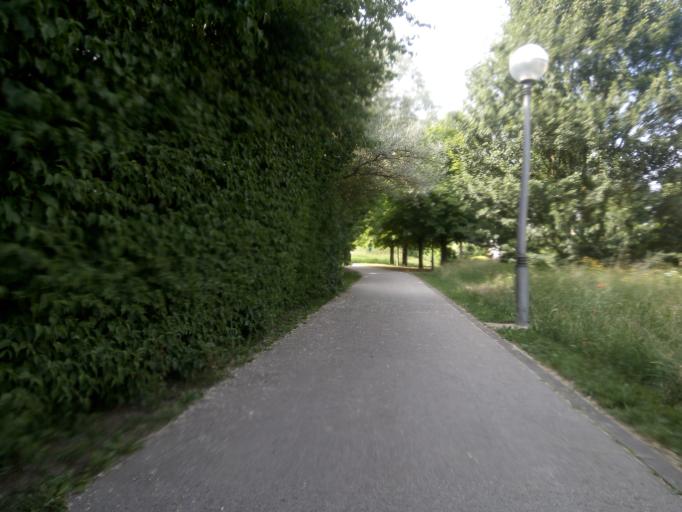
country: LU
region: Luxembourg
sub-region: Canton d'Esch-sur-Alzette
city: Esch-sur-Alzette
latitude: 49.5095
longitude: 5.9781
